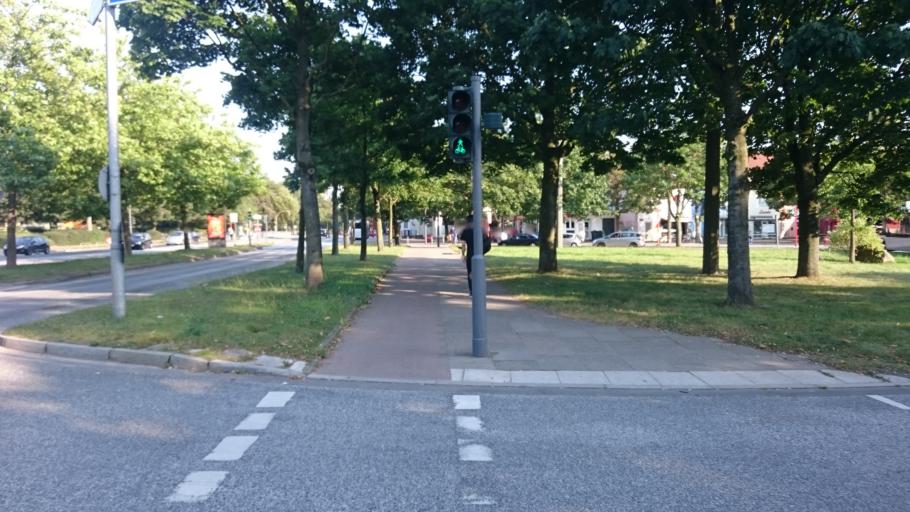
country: DE
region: Hamburg
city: Eidelstedt
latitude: 53.5740
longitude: 9.8916
